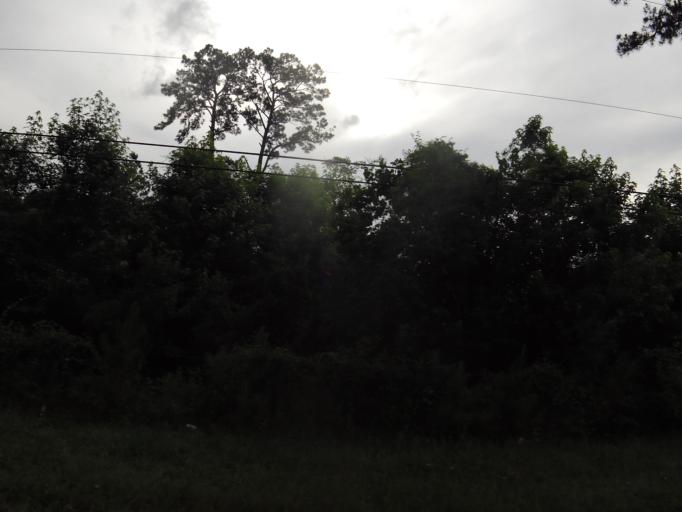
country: US
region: Florida
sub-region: Nassau County
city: Nassau Village-Ratliff
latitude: 30.5158
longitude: -81.7479
